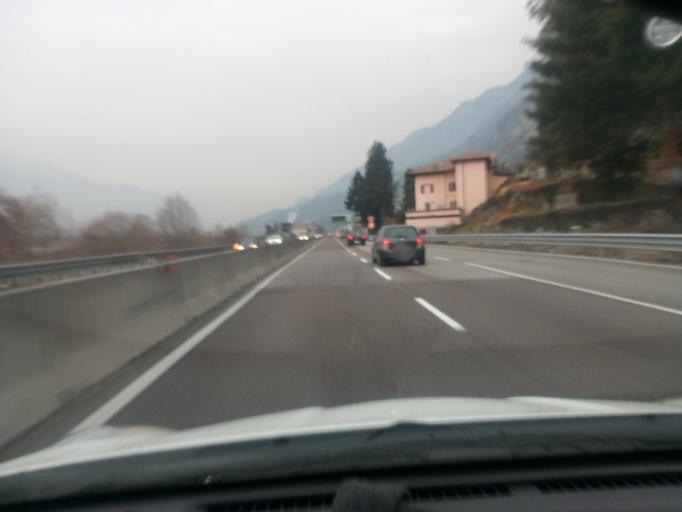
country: IT
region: Trentino-Alto Adige
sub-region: Provincia di Trento
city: Trento
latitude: 46.0642
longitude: 11.1113
